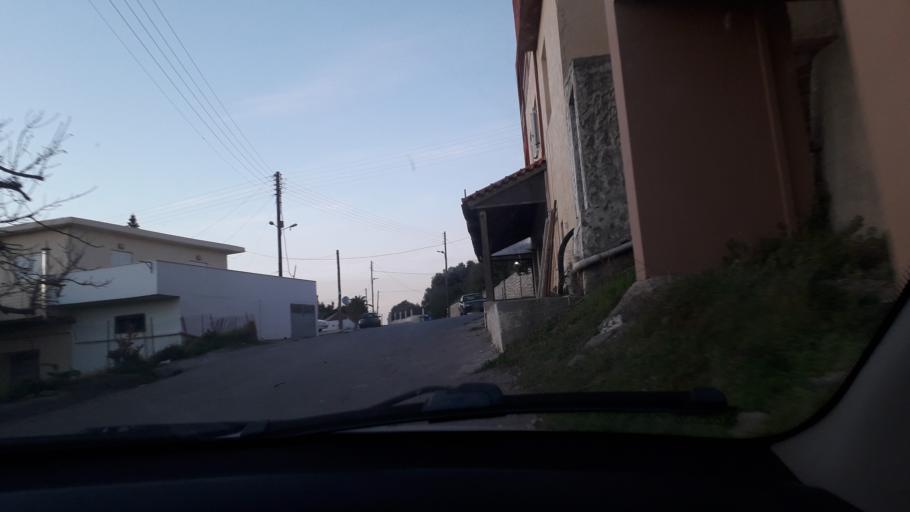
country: GR
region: Crete
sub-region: Nomos Rethymnis
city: Panormos
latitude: 35.3832
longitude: 24.6194
